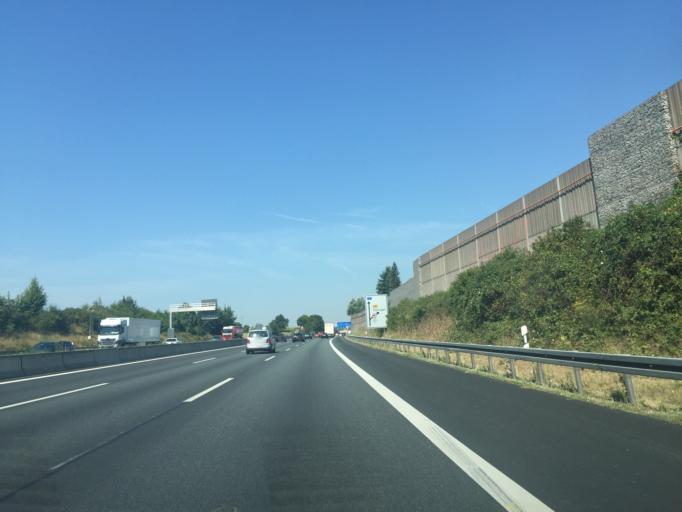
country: DE
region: Baden-Wuerttemberg
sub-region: Karlsruhe Region
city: Sinsheim
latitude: 49.2451
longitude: 8.8694
